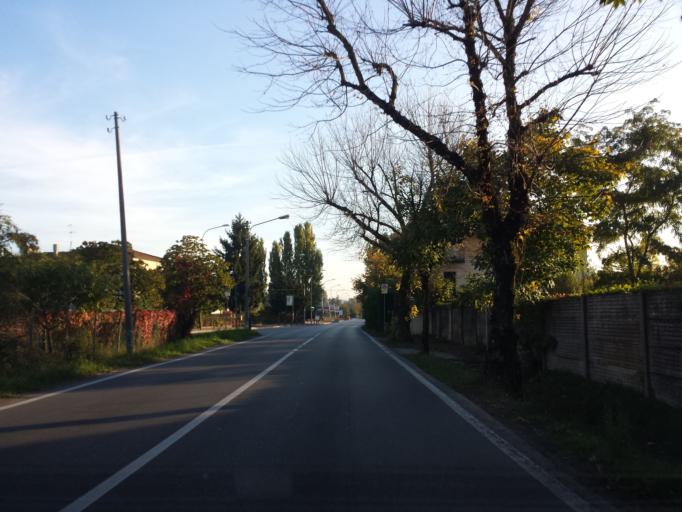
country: IT
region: Veneto
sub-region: Provincia di Vicenza
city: Vicenza
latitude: 45.5735
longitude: 11.5361
